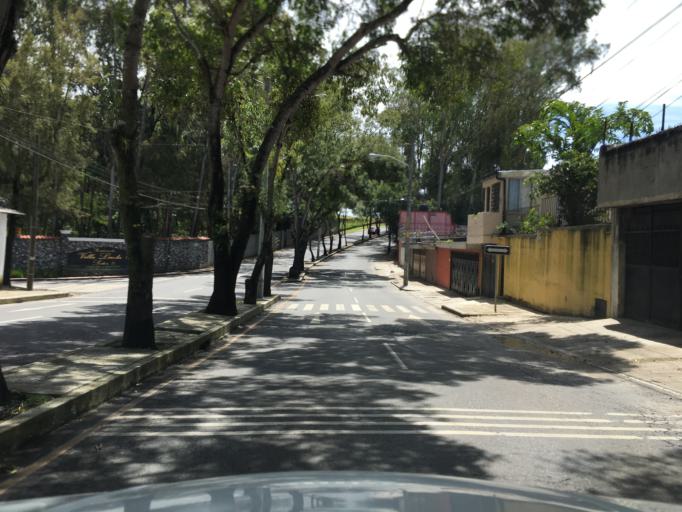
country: GT
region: Guatemala
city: Guatemala City
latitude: 14.6429
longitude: -90.5519
